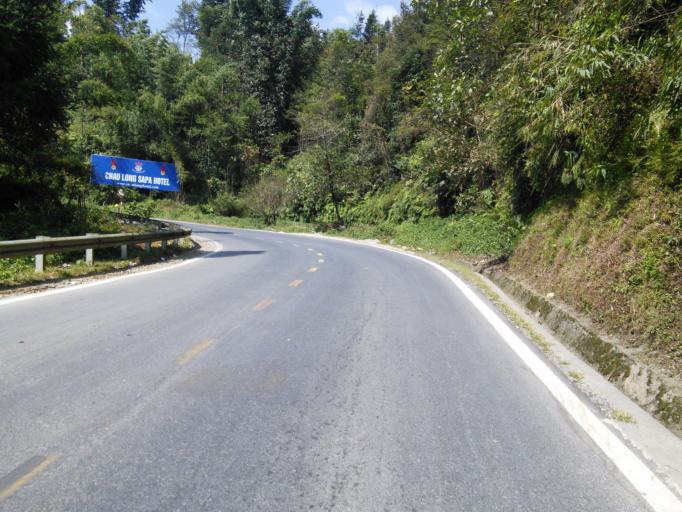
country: VN
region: Lao Cai
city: Sa Pa
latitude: 22.3553
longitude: 103.8610
